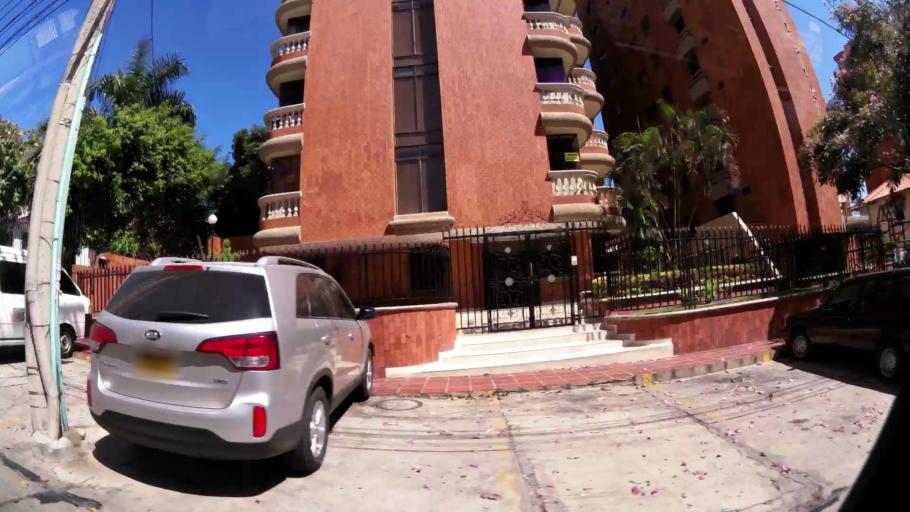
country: CO
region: Atlantico
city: Barranquilla
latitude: 11.0039
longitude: -74.8096
